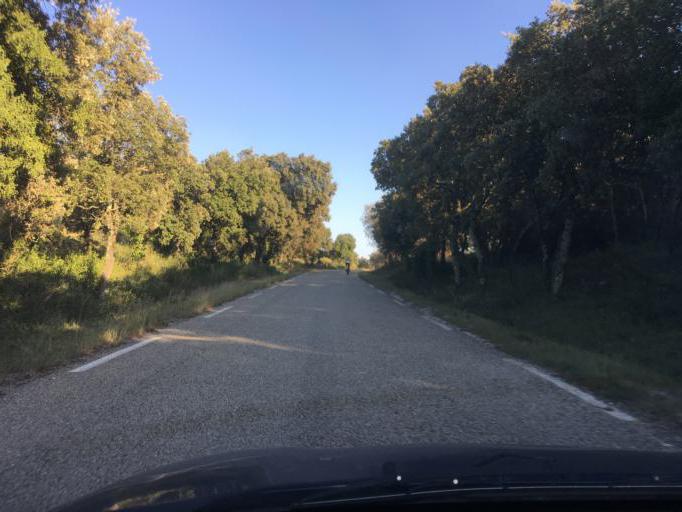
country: FR
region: Languedoc-Roussillon
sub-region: Departement du Gard
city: Saint-Victor-la-Coste
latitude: 44.0090
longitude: 4.6047
